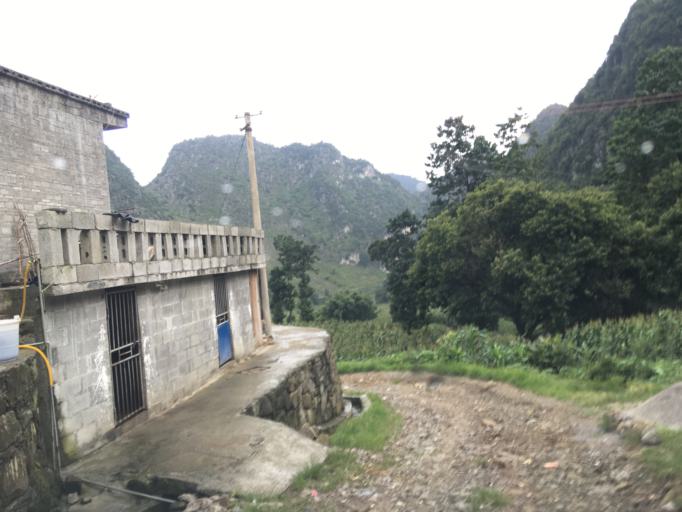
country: CN
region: Guangxi Zhuangzu Zizhiqu
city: Xinzhou
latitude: 24.9890
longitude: 105.6403
